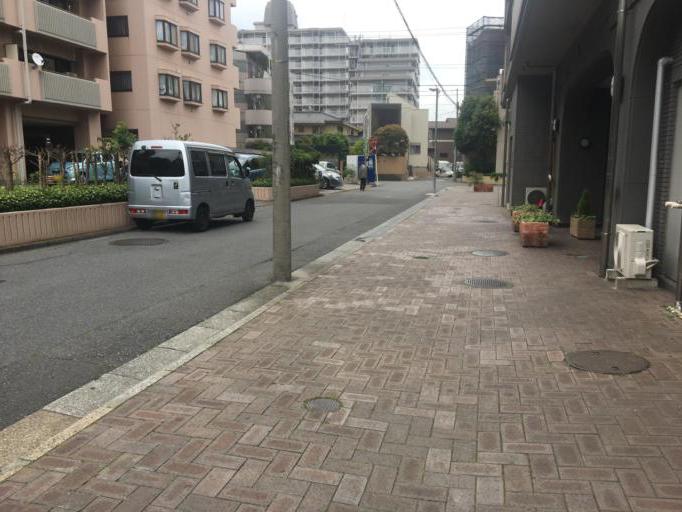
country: JP
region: Saitama
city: Kawaguchi
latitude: 35.7965
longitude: 139.7153
